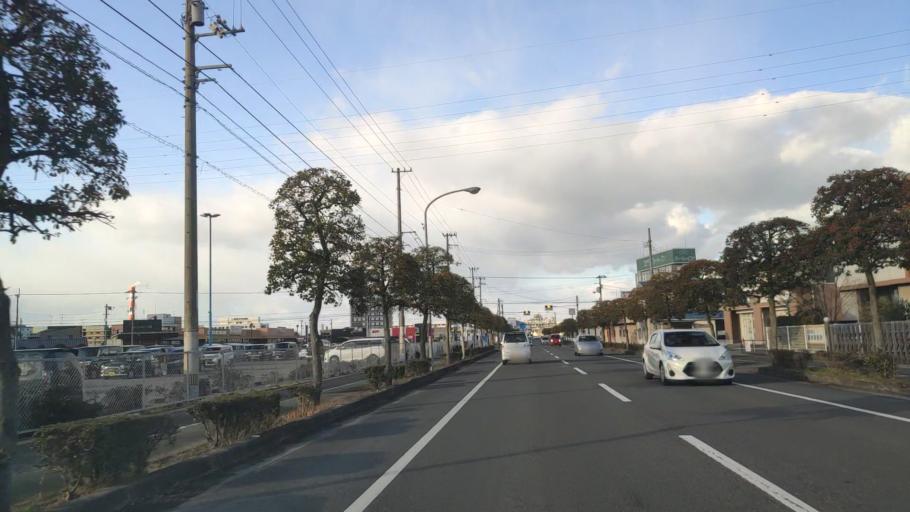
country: JP
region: Ehime
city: Saijo
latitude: 33.9251
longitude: 133.1838
